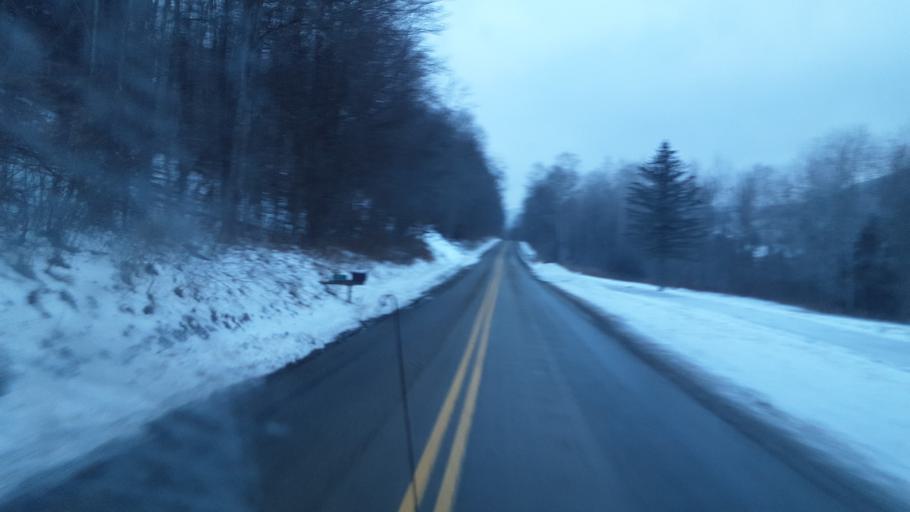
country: US
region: New York
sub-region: Allegany County
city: Wellsville
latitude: 41.9698
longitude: -77.8508
